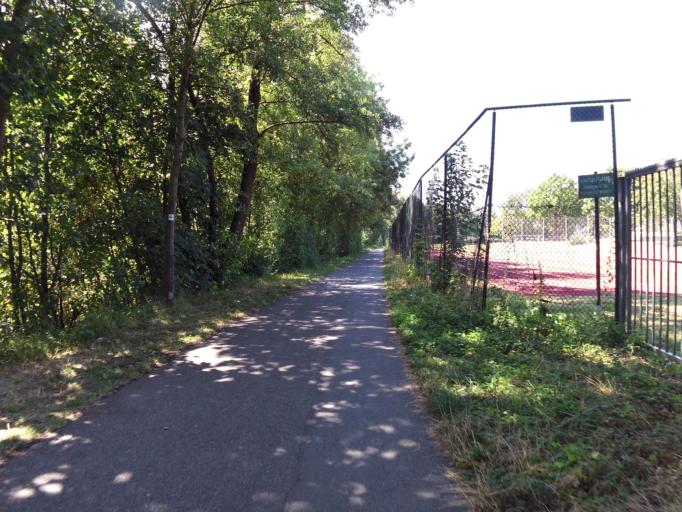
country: DE
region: Baden-Wuerttemberg
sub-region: Karlsruhe Region
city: Mosbach
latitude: 49.3475
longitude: 9.1323
